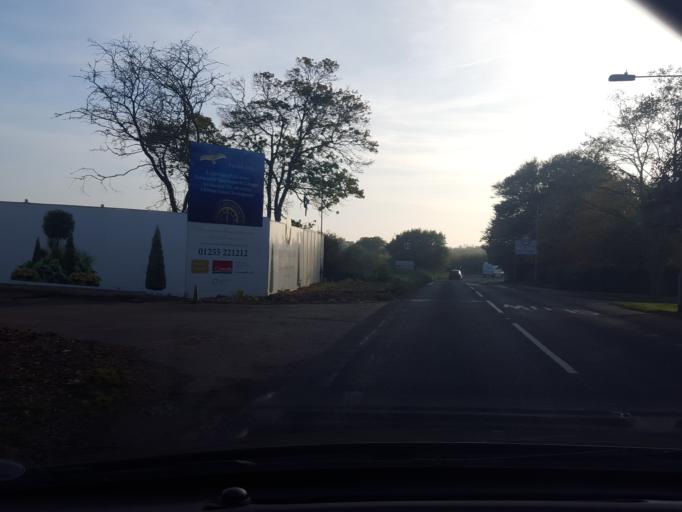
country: GB
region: England
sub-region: Essex
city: Frinton-on-Sea
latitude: 51.8399
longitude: 1.2184
